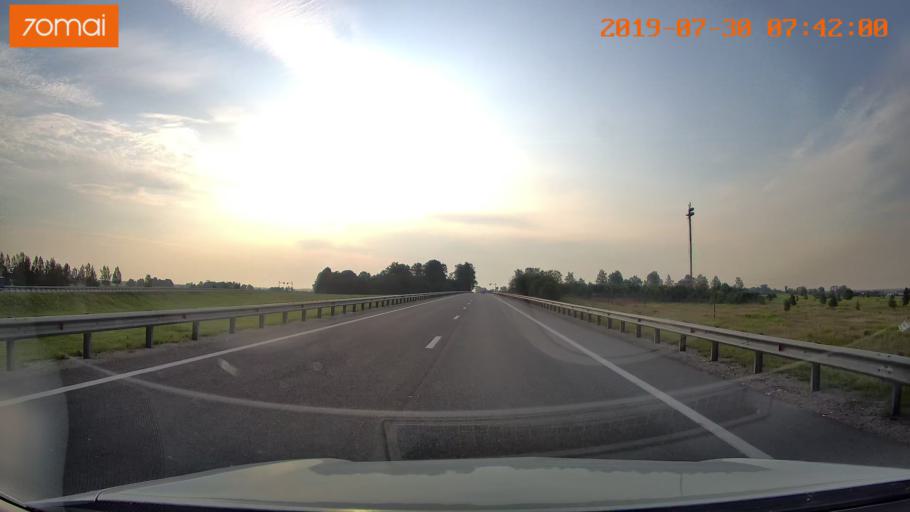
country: RU
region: Kaliningrad
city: Gvardeysk
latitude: 54.6478
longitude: 21.2668
